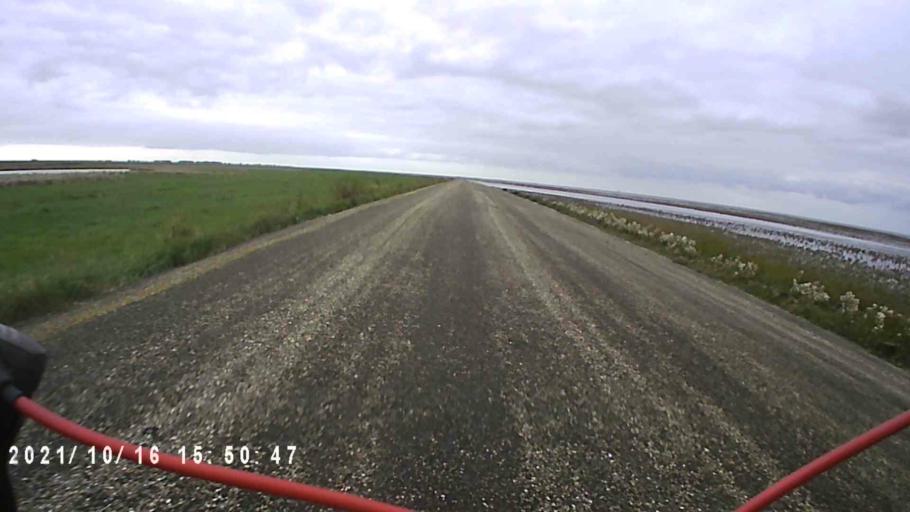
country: NL
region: Friesland
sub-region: Gemeente Dongeradeel
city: Anjum
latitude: 53.4038
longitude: 6.1361
